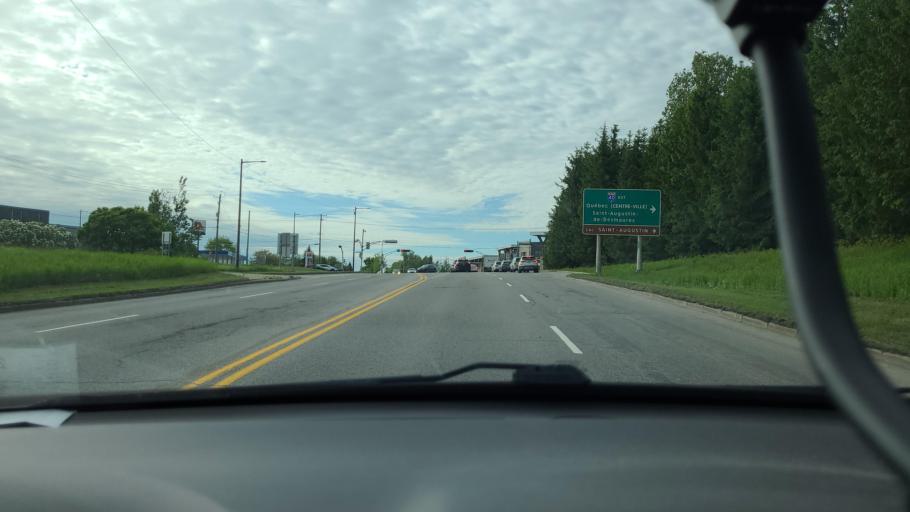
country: CA
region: Quebec
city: L'Ancienne-Lorette
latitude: 46.7657
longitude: -71.3720
